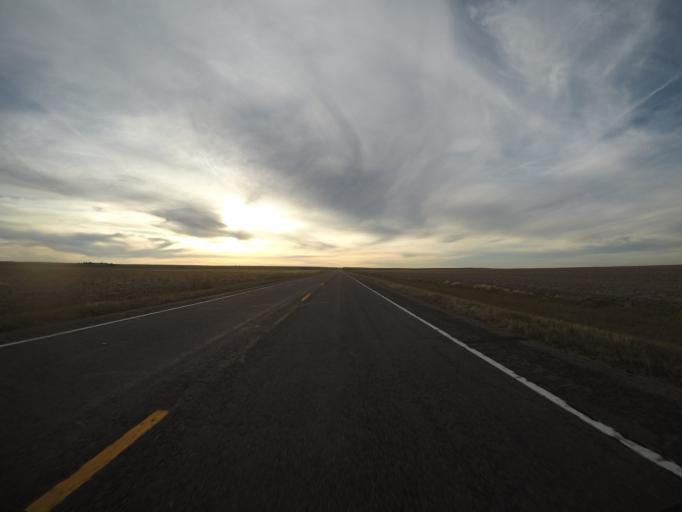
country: US
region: Colorado
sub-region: Yuma County
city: Yuma
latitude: 39.6991
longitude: -103.0029
